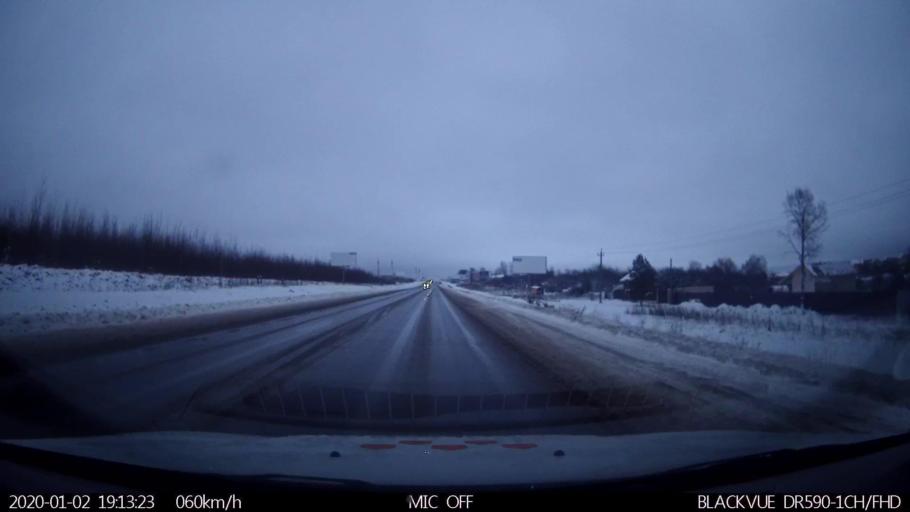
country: RU
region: Nizjnij Novgorod
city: Burevestnik
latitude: 56.2023
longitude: 43.8536
